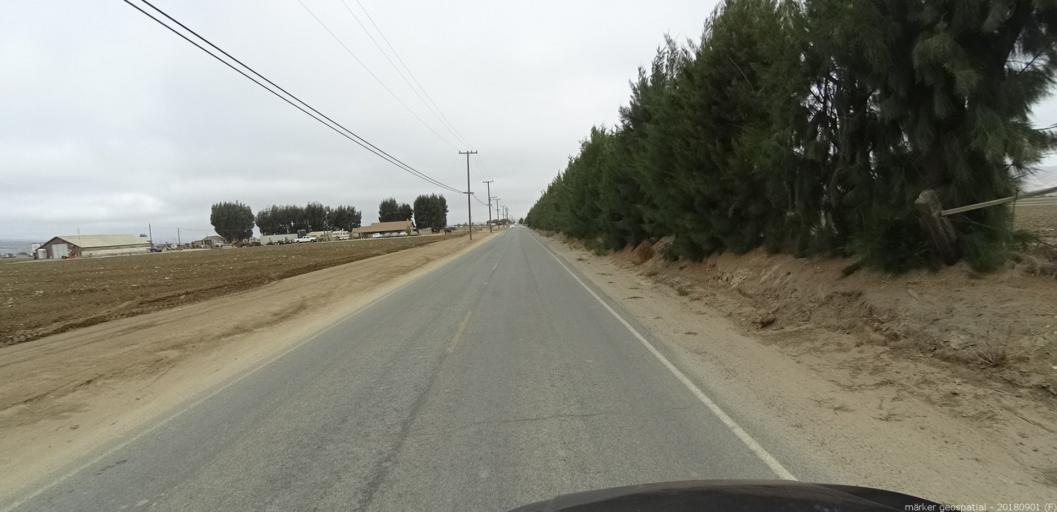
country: US
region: California
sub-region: Monterey County
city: Soledad
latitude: 36.3825
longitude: -121.3296
